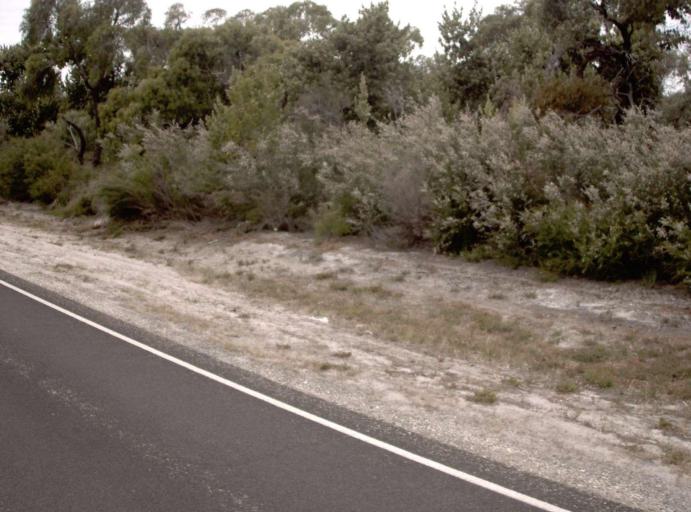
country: AU
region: Victoria
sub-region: Wellington
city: Sale
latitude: -38.1833
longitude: 147.3738
